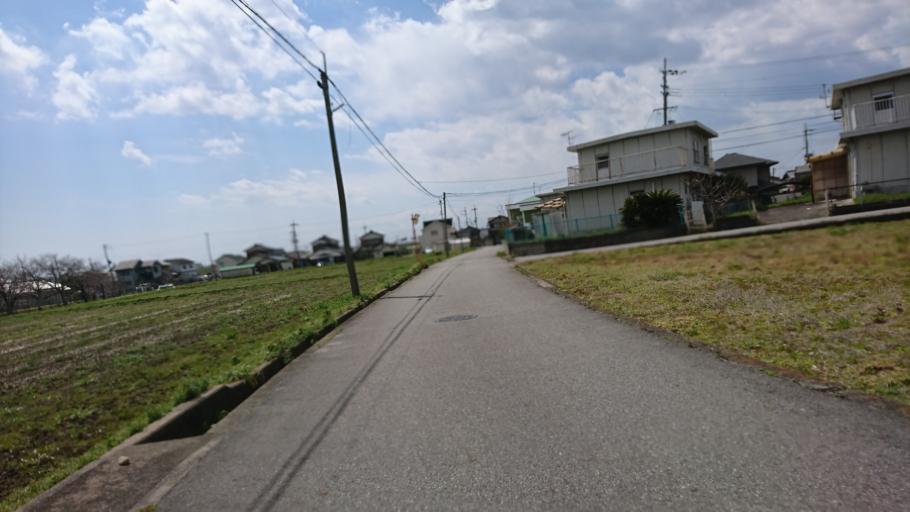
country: JP
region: Hyogo
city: Kakogawacho-honmachi
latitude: 34.7548
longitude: 134.8986
